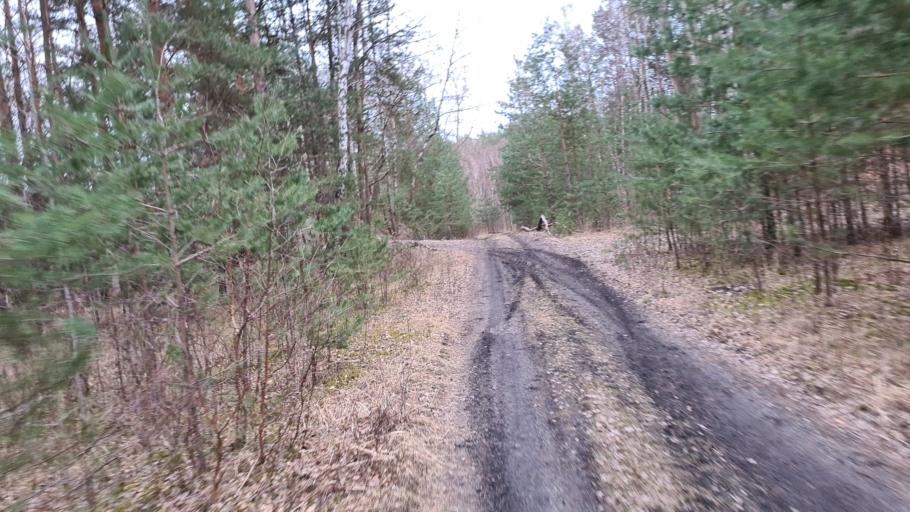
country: DE
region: Brandenburg
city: Trobitz
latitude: 51.5959
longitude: 13.4611
